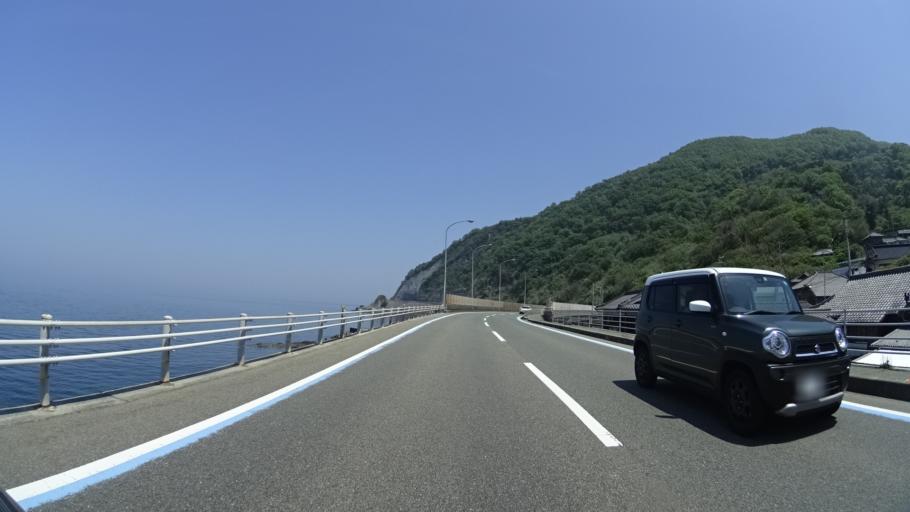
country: JP
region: Ehime
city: Ozu
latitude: 33.5890
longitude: 132.4561
